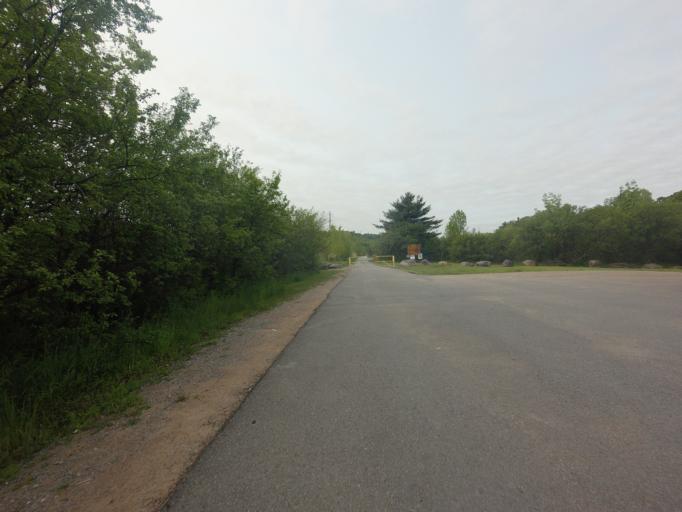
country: US
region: New York
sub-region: Jefferson County
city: Black River
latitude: 44.0032
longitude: -75.8047
